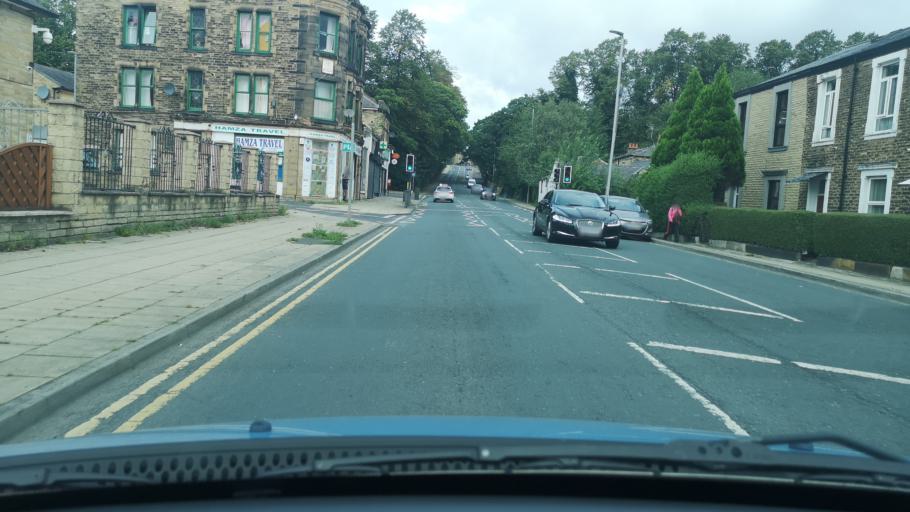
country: GB
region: England
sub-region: Kirklees
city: Batley
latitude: 53.6977
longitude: -1.6392
